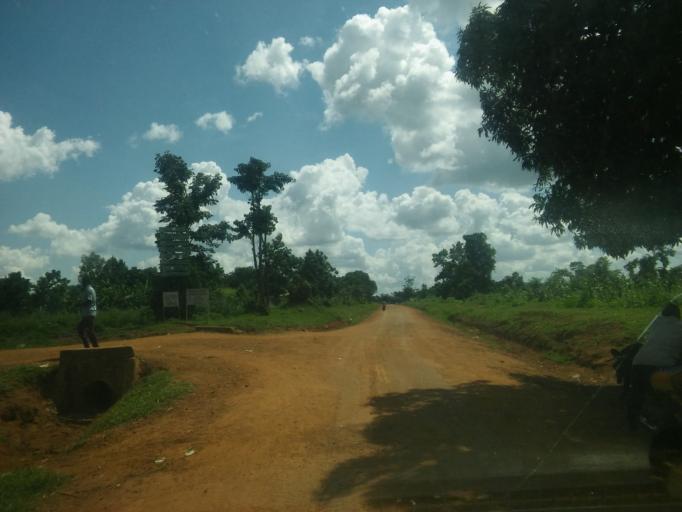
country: UG
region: Eastern Region
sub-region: Pallisa District
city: Pallisa
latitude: 1.1511
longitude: 33.8109
